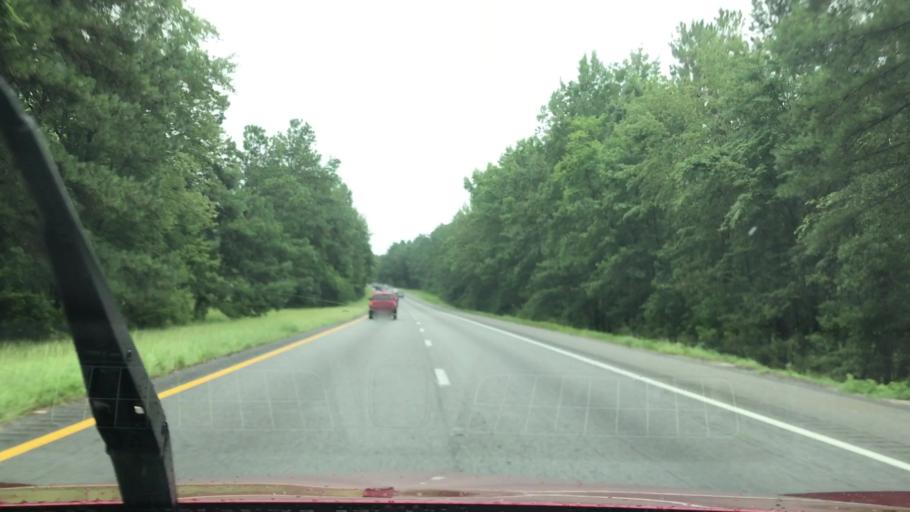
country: US
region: South Carolina
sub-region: Dorchester County
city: Ridgeville
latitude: 33.1577
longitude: -80.3510
